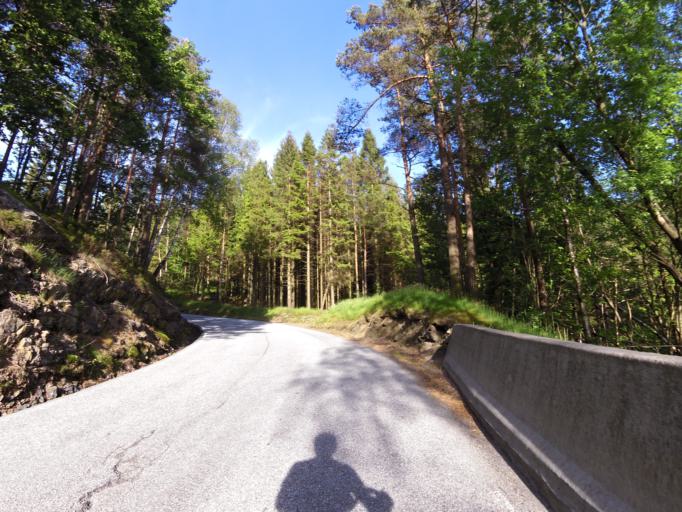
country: NO
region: Vest-Agder
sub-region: Flekkefjord
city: Flekkefjord
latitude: 58.2785
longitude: 6.6374
